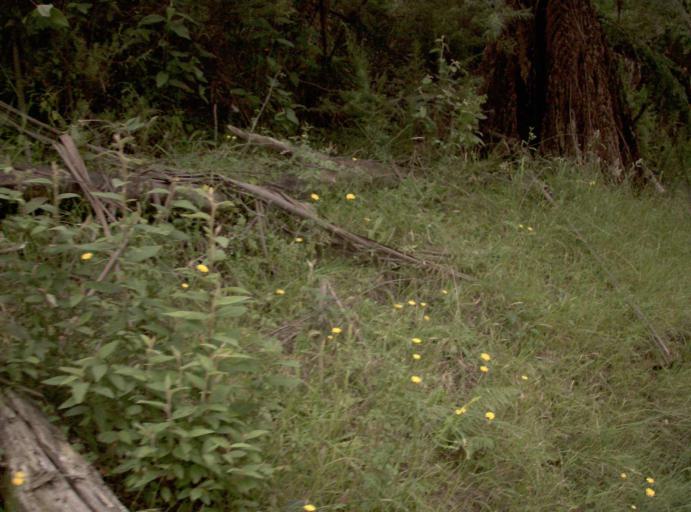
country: AU
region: Victoria
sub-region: Yarra Ranges
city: Healesville
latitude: -37.6041
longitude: 145.6205
